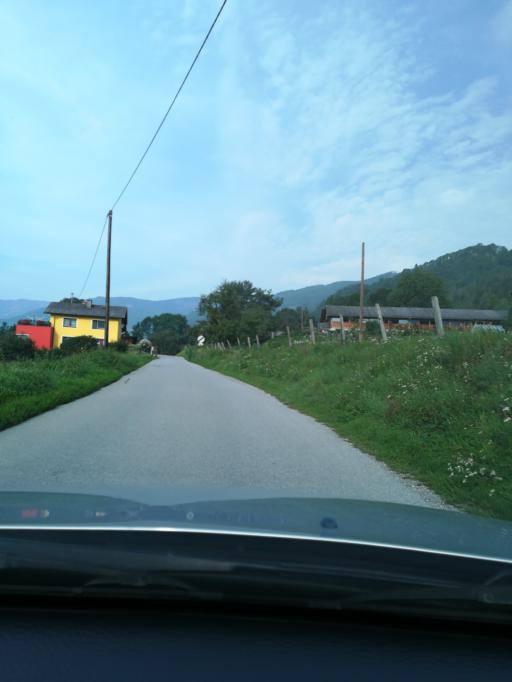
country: AT
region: Styria
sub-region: Politischer Bezirk Murtal
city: Sankt Georgen ob Judenburg
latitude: 47.2161
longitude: 14.4885
